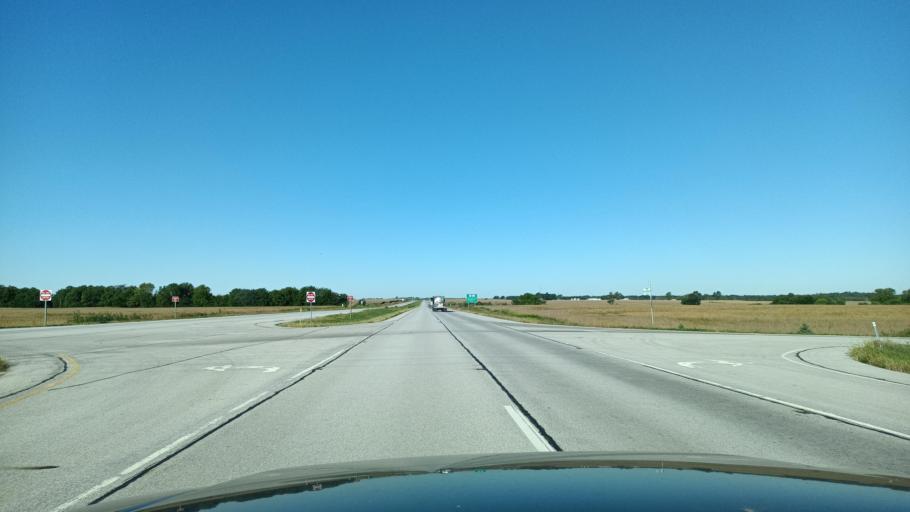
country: US
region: Illinois
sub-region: Henderson County
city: Oquawka
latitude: 40.8435
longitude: -90.8736
